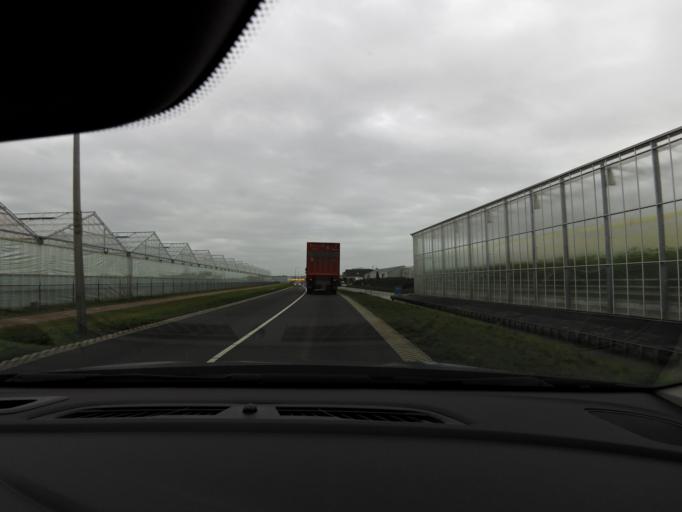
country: NL
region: South Holland
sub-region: Gemeente Westland
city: De Lier
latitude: 51.9582
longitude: 4.2506
